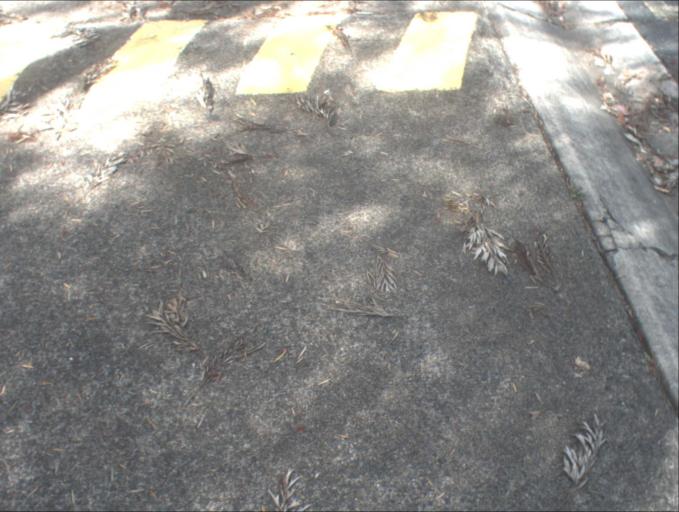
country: AU
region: Queensland
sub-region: Logan
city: Park Ridge South
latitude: -27.6704
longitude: 153.0348
